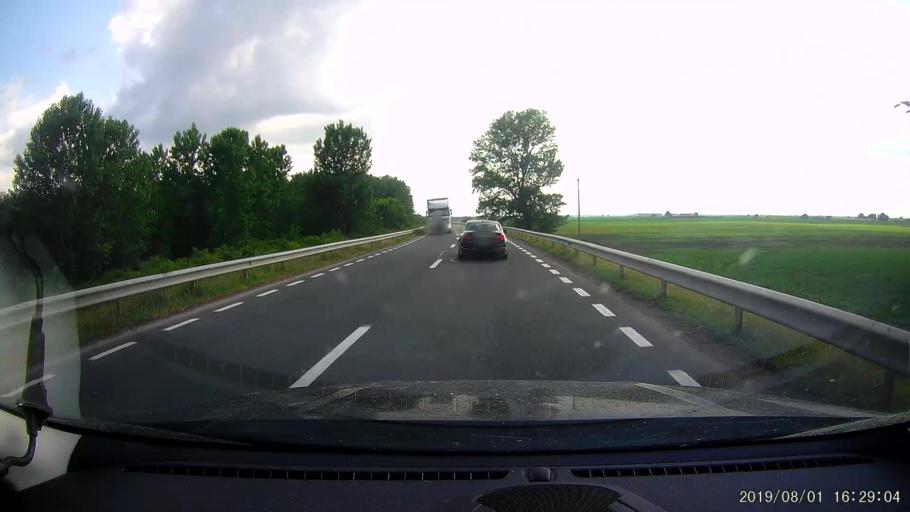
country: BG
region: Silistra
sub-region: Obshtina Silistra
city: Silistra
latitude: 44.1452
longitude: 27.2950
